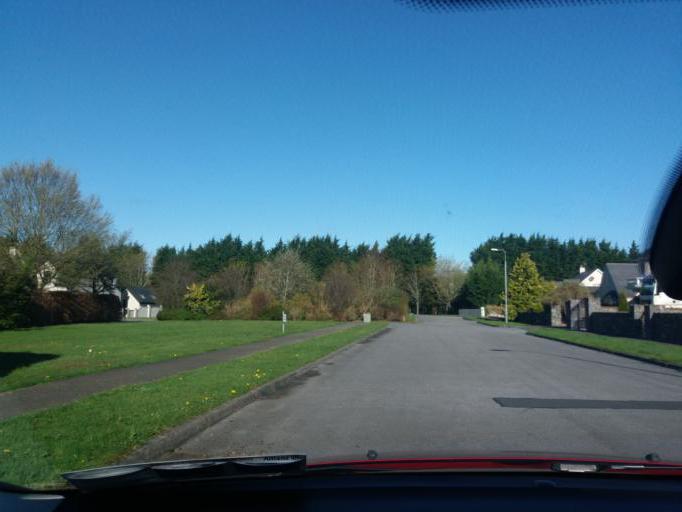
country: IE
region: Munster
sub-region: Ciarrai
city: Cill Airne
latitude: 52.0514
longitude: -9.5179
